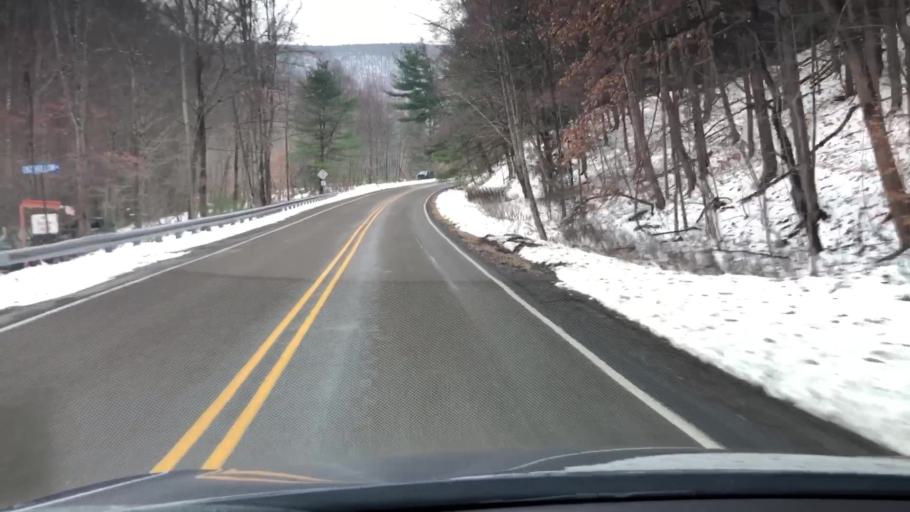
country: US
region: Pennsylvania
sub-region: Cameron County
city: Emporium
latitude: 41.3413
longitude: -78.2950
